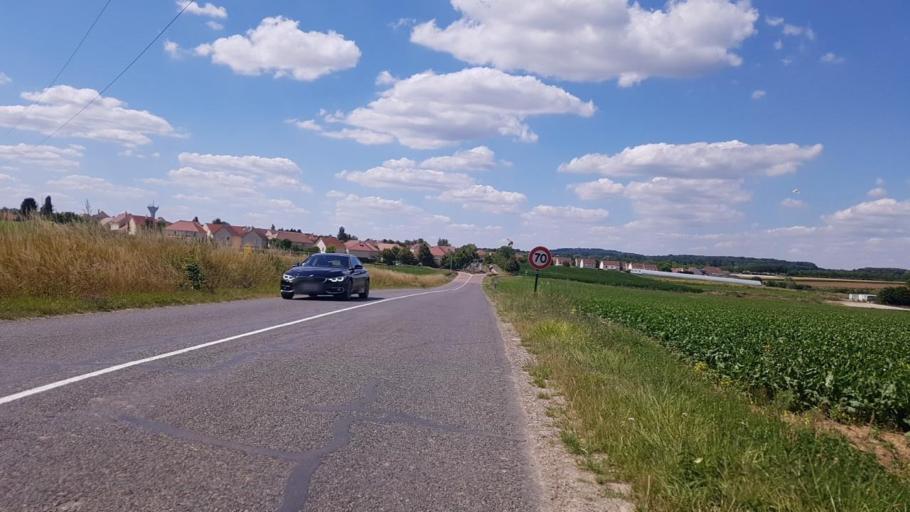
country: FR
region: Ile-de-France
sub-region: Departement de Seine-et-Marne
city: Moussy-le-Neuf
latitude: 49.0572
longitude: 2.6135
